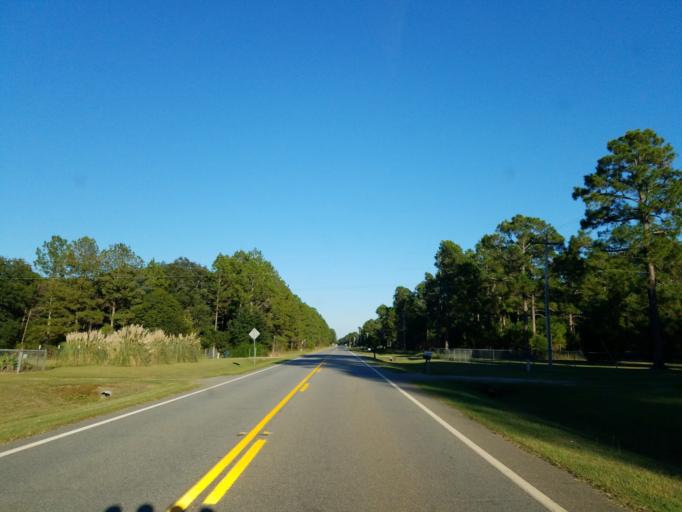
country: US
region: Georgia
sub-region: Lee County
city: Leesburg
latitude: 31.7271
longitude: -84.0544
